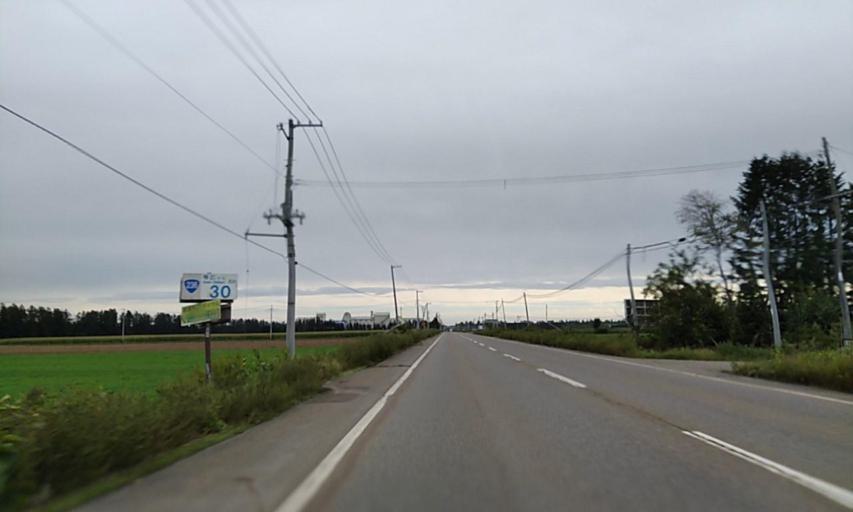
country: JP
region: Hokkaido
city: Obihiro
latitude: 42.6861
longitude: 143.1354
